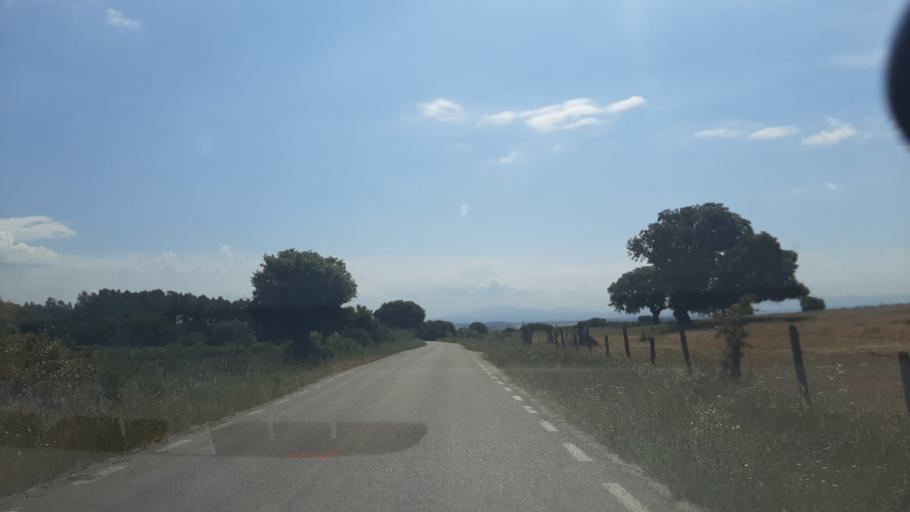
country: ES
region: Castille and Leon
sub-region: Provincia de Salamanca
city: Gallegos de Arganan
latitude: 40.6424
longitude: -6.7366
